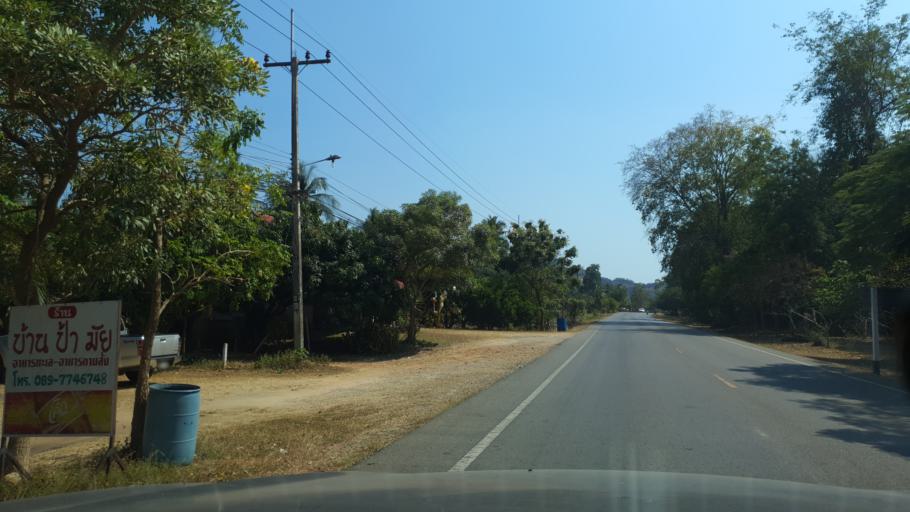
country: TH
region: Prachuap Khiri Khan
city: Sam Roi Yot
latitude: 12.2147
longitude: 99.9758
